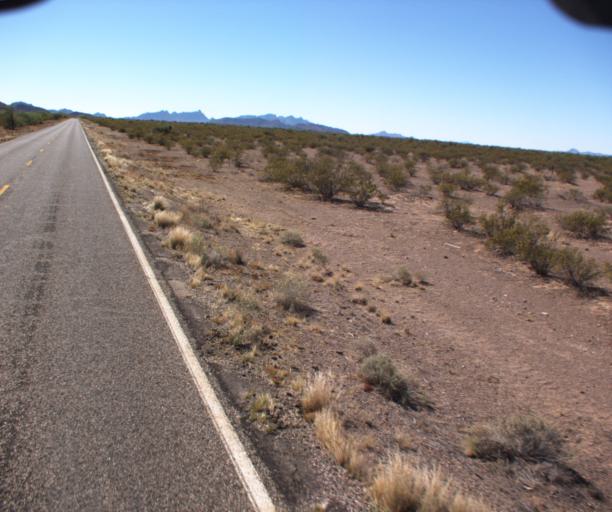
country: US
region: Arizona
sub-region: Pima County
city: Ajo
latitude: 32.3131
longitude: -112.7650
